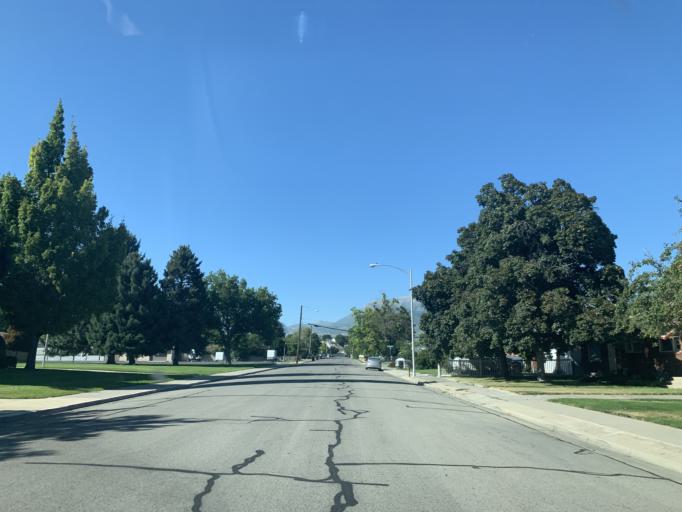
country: US
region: Utah
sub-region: Utah County
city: Provo
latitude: 40.2546
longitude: -111.6820
